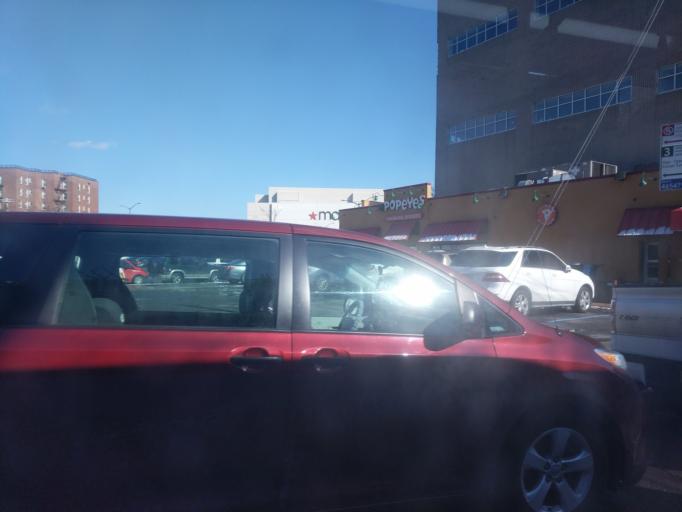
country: US
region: New York
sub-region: Queens County
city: Borough of Queens
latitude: 40.7339
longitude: -73.8739
